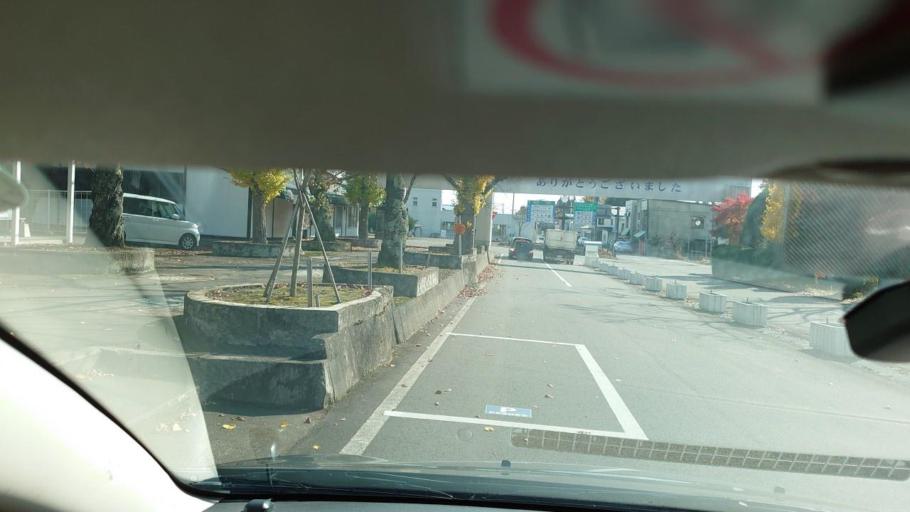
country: JP
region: Iwate
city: Hanamaki
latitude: 39.4513
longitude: 141.0707
